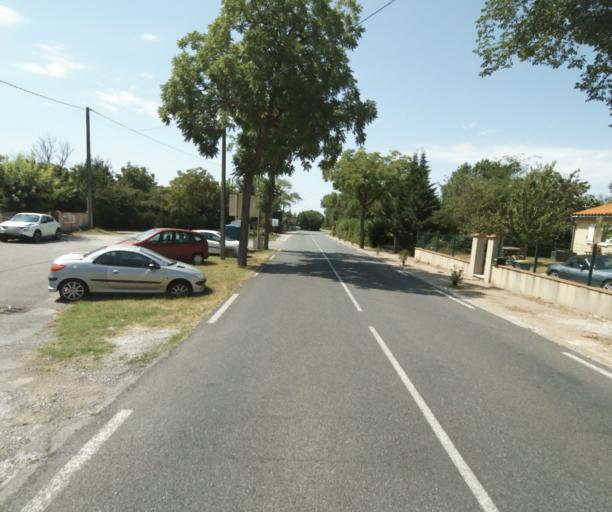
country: FR
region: Midi-Pyrenees
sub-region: Departement de la Haute-Garonne
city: Saint-Felix-Lauragais
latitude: 43.4510
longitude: 1.8816
